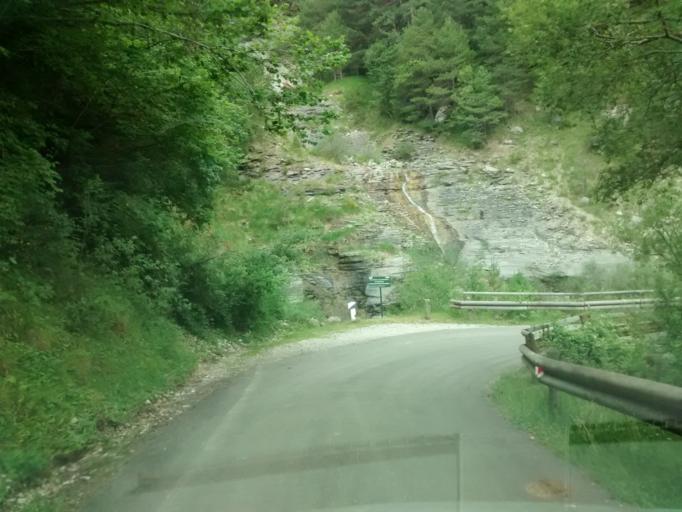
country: ES
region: Aragon
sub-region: Provincia de Huesca
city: Puertolas
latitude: 42.5907
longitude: 0.1262
